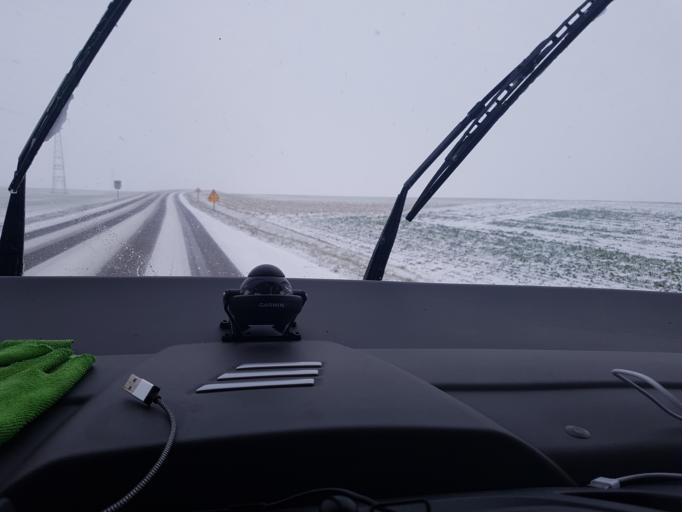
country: FR
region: Lorraine
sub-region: Departement de la Moselle
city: Chateau-Salins
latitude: 48.8390
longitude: 6.4682
